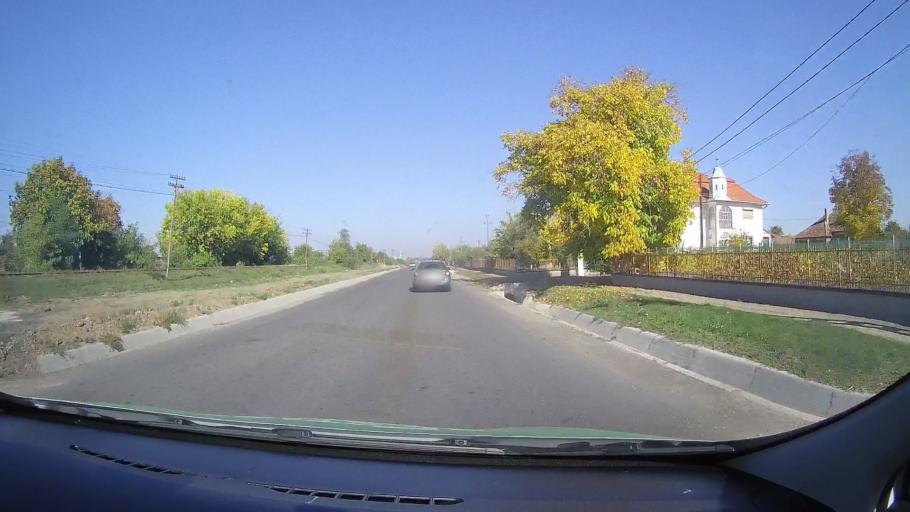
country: RO
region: Satu Mare
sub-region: Comuna Berveni
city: Lucaceni
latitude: 47.7419
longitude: 22.4746
